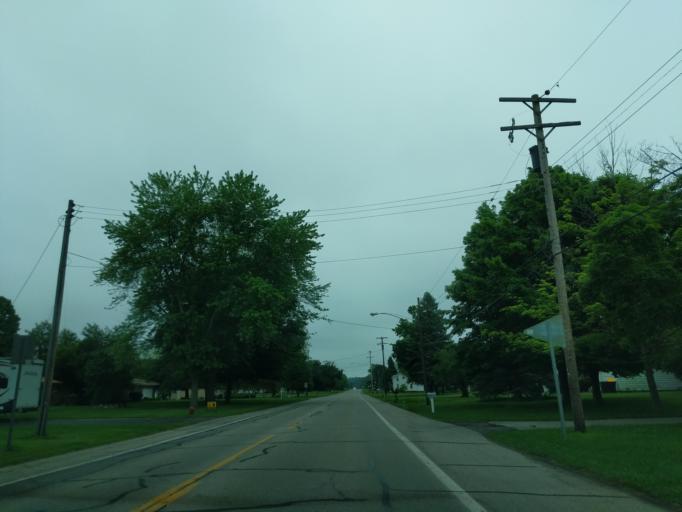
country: US
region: Michigan
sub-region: Hillsdale County
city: Litchfield
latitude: 42.0404
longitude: -84.7508
